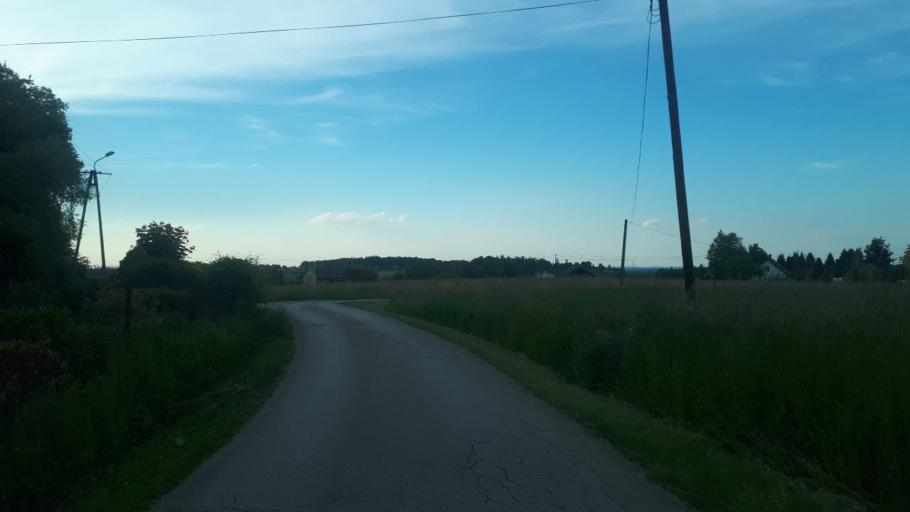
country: PL
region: Silesian Voivodeship
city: Janowice
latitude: 49.8868
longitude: 19.1026
